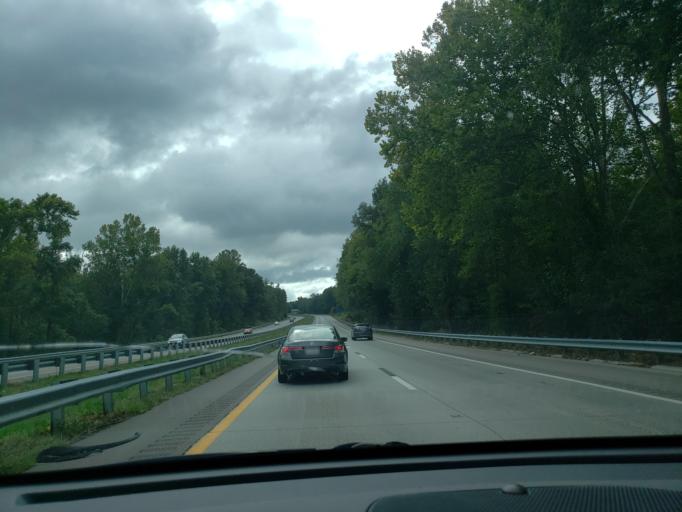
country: US
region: North Carolina
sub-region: Vance County
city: Henderson
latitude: 36.4156
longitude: -78.3171
